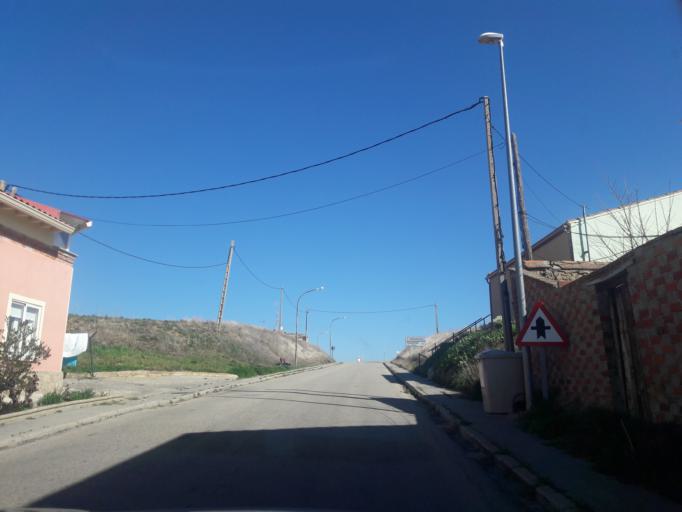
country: ES
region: Castille and Leon
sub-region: Provincia de Salamanca
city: Mancera de Abajo
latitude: 40.8420
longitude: -5.1990
